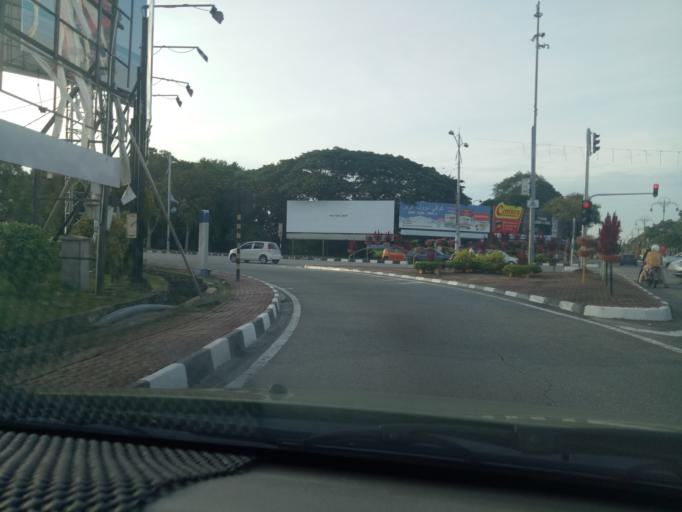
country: MY
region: Kedah
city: Alor Setar
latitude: 6.1434
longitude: 100.3702
